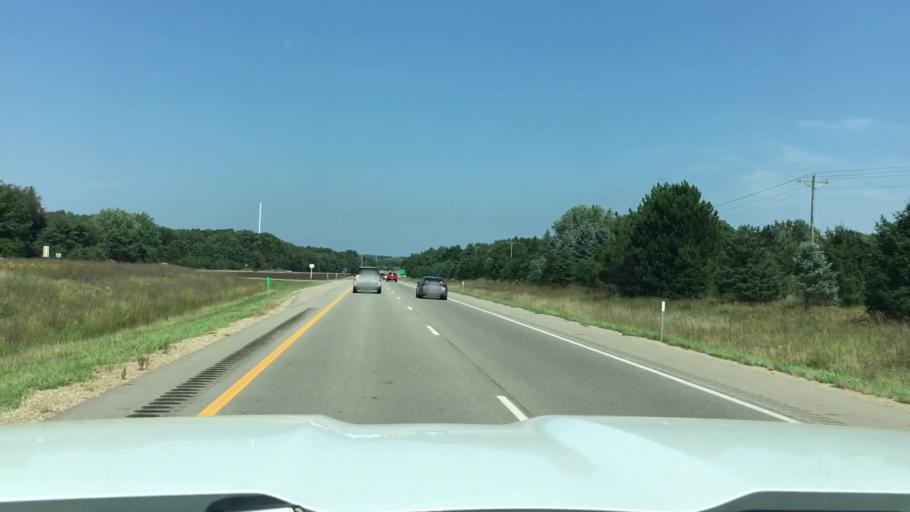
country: US
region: Michigan
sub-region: Kalamazoo County
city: Portage
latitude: 42.1889
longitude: -85.6460
